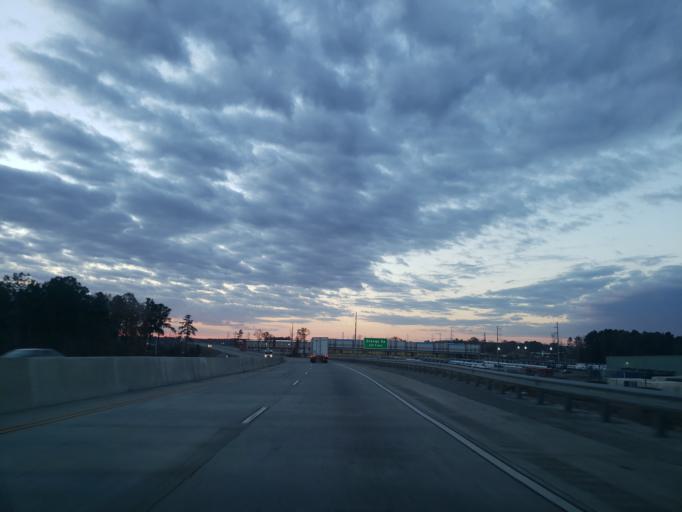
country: US
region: Georgia
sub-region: Chatham County
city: Port Wentworth
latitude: 32.1526
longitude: -81.1759
